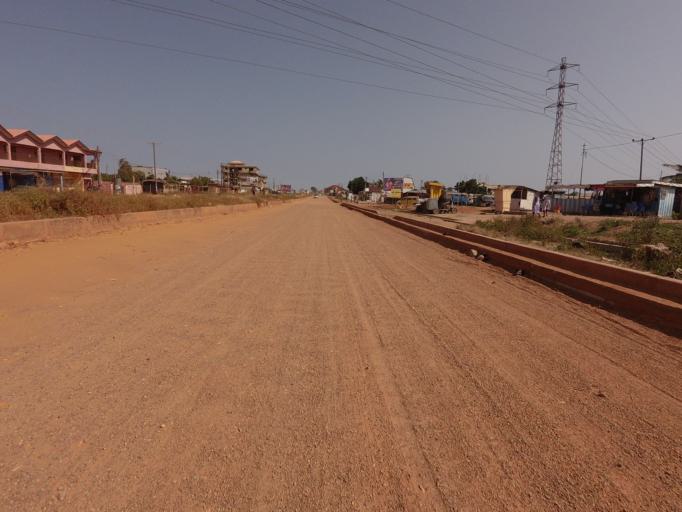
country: GH
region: Greater Accra
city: Teshi Old Town
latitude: 5.6155
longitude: -0.1246
